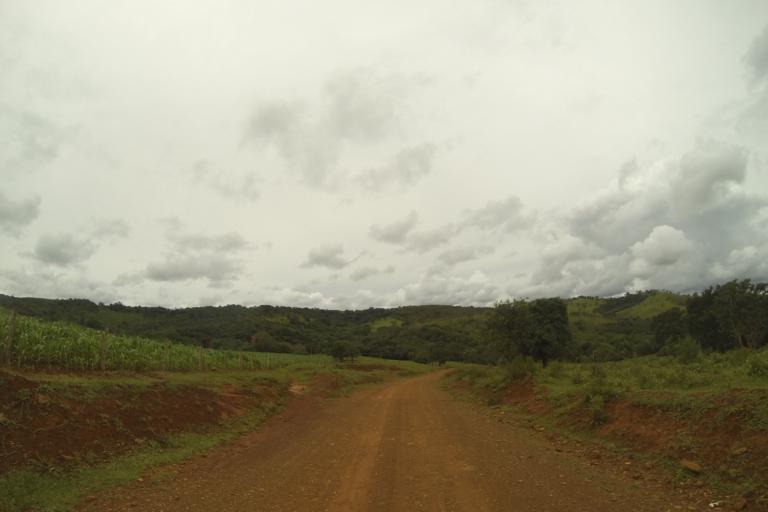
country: BR
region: Minas Gerais
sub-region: Ibia
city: Ibia
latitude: -19.6565
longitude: -46.7008
